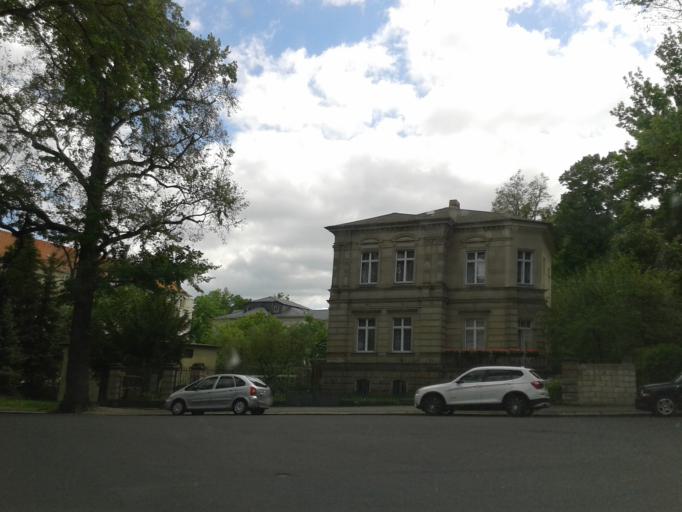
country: DE
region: Saxony
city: Dresden
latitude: 51.0364
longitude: 13.7280
